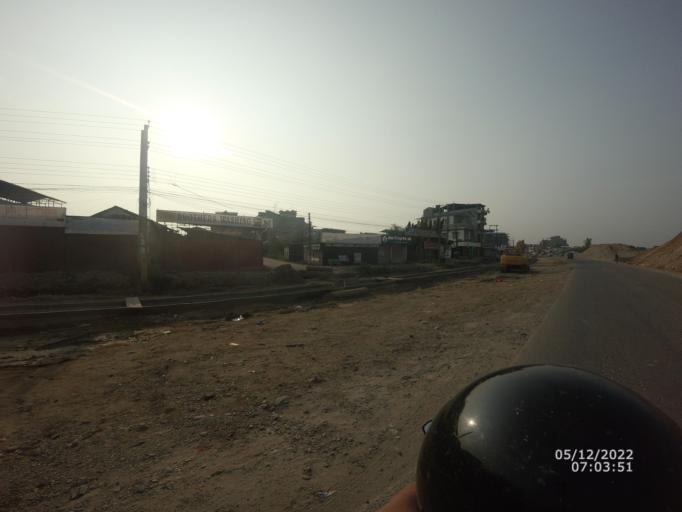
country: NP
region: Central Region
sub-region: Narayani Zone
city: Bharatpur
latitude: 27.6746
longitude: 84.4315
